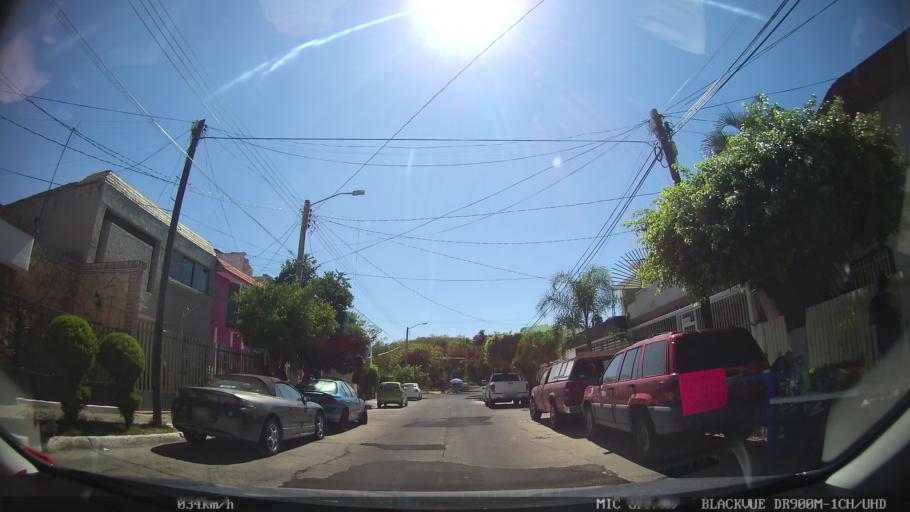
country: MX
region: Jalisco
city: Tlaquepaque
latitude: 20.6456
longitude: -103.2933
